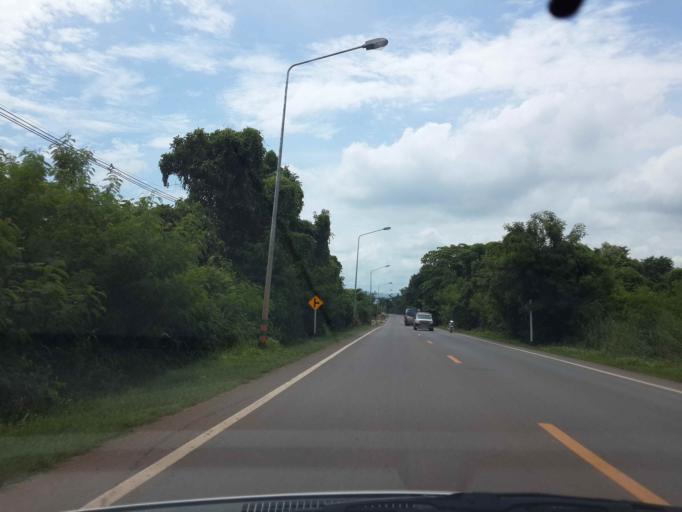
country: TH
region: Ratchaburi
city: Pak Tho
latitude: 13.3637
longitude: 99.7559
